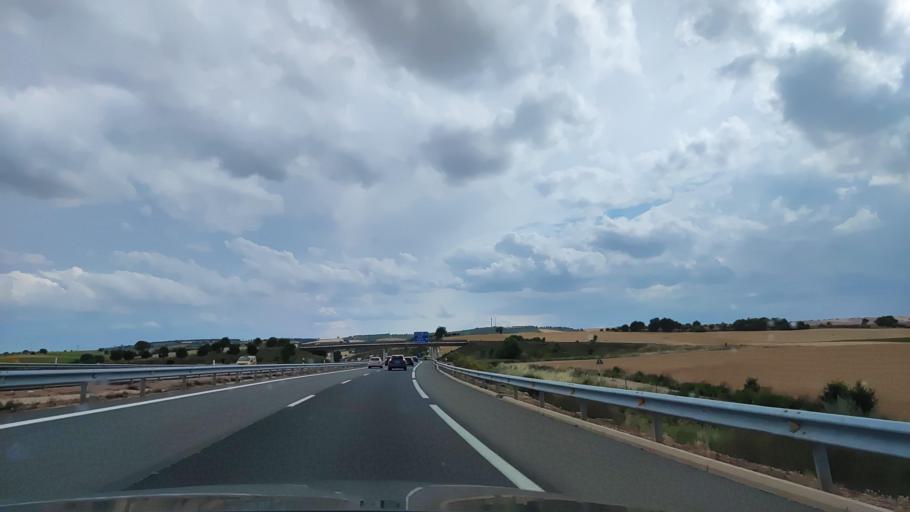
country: ES
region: Castille-La Mancha
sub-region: Provincia de Cuenca
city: Castillo de Garcimunoz
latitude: 39.6963
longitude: -2.3890
